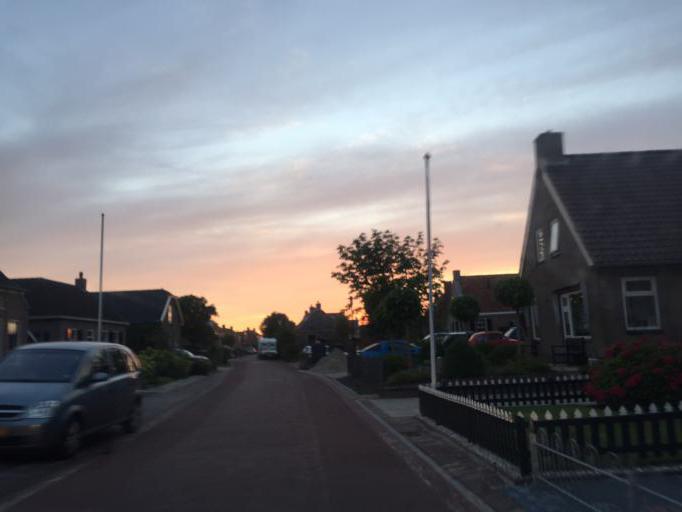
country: NL
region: Friesland
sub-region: Gemeente Dongeradeel
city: Anjum
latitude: 53.4031
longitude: 6.0816
